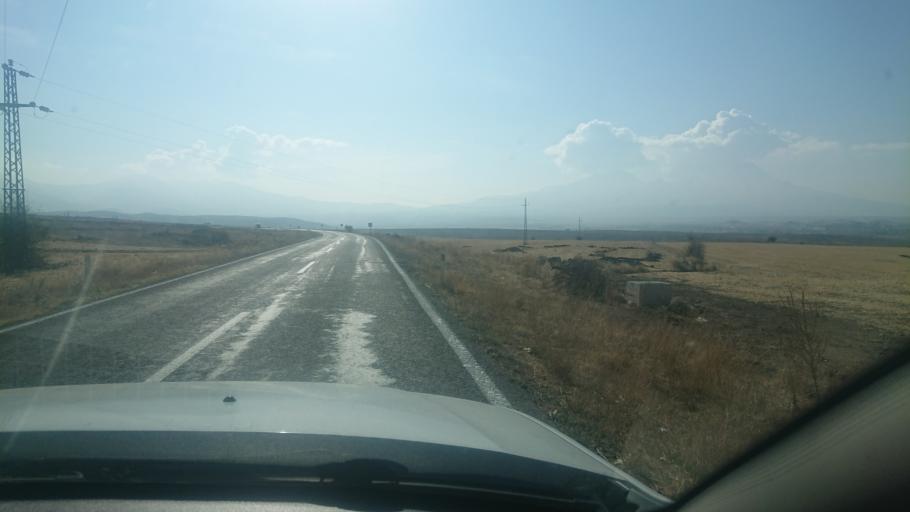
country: TR
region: Aksaray
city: Guzelyurt
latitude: 38.2625
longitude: 34.3317
